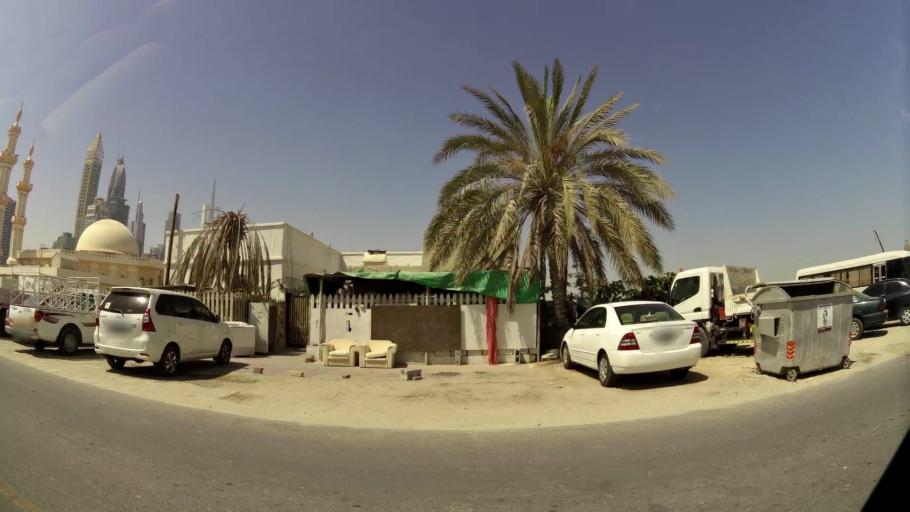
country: AE
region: Ash Shariqah
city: Sharjah
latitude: 25.2206
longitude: 55.2743
